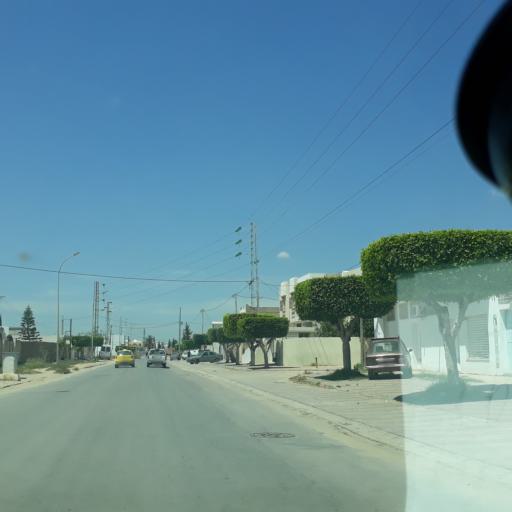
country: TN
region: Safaqis
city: Al Qarmadah
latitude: 34.8146
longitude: 10.7464
